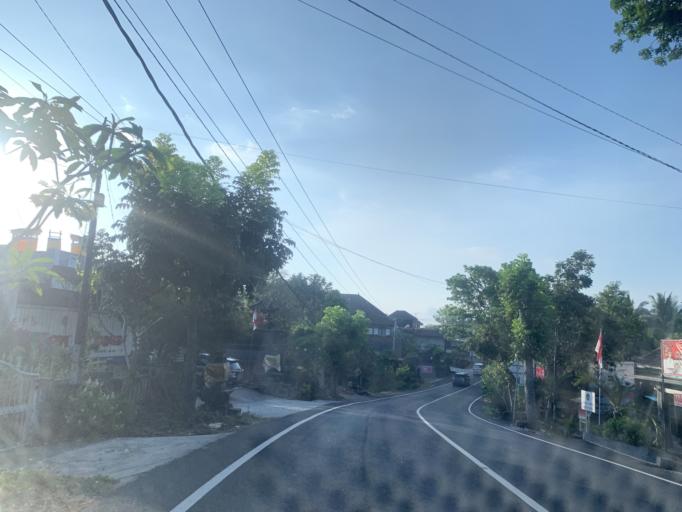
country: ID
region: Bali
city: Banjar Delodrurung
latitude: -8.4941
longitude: 114.9627
